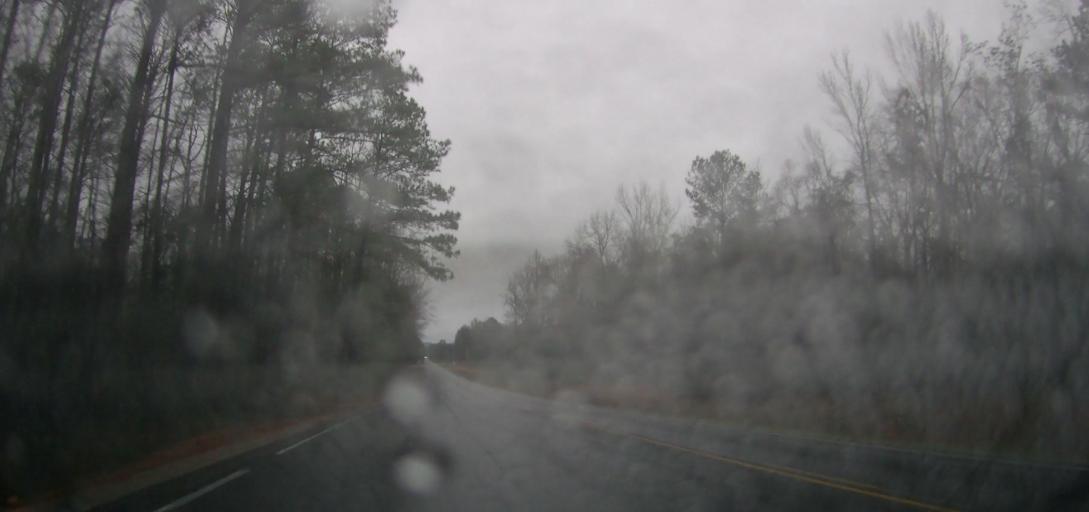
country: US
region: Alabama
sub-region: Autauga County
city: Pine Level
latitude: 32.5762
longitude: -86.6850
